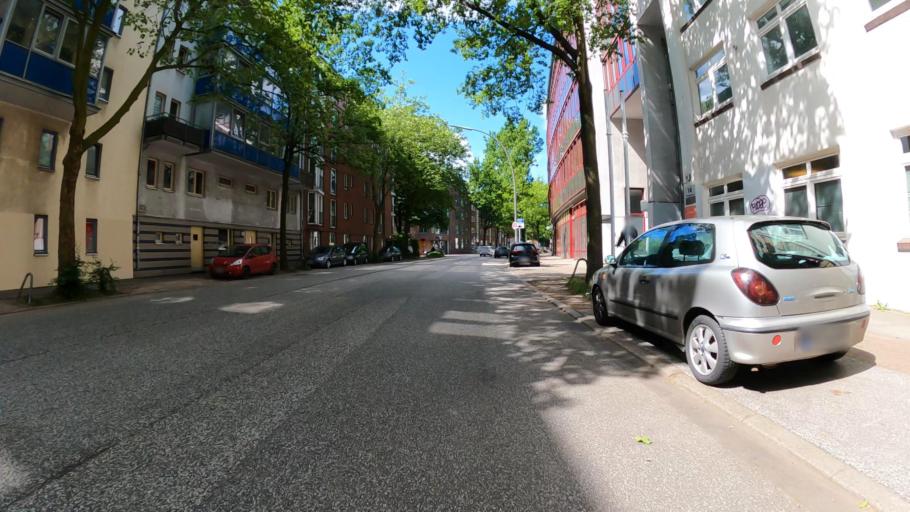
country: DE
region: Hamburg
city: Altona
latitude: 53.5548
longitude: 9.9255
